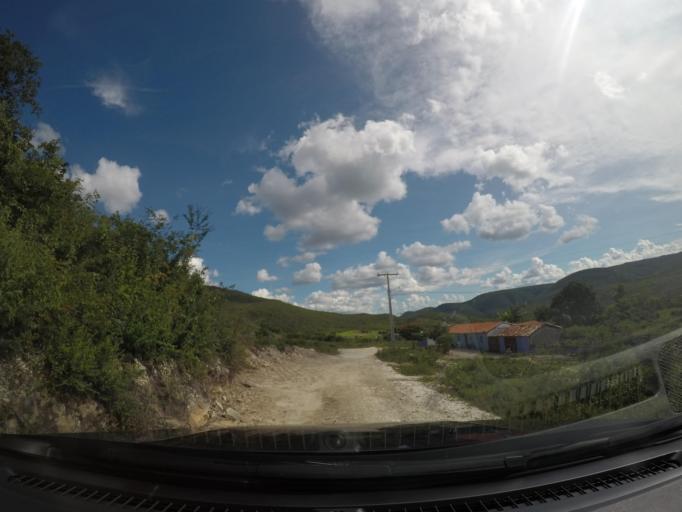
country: BR
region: Bahia
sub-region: Barra Da Estiva
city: Barra da Estiva
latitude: -13.1256
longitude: -41.5944
